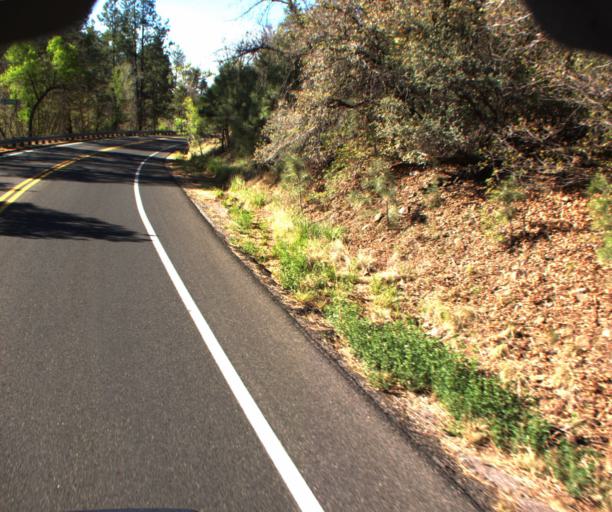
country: US
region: Arizona
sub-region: Yavapai County
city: Prescott
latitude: 34.5176
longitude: -112.4777
